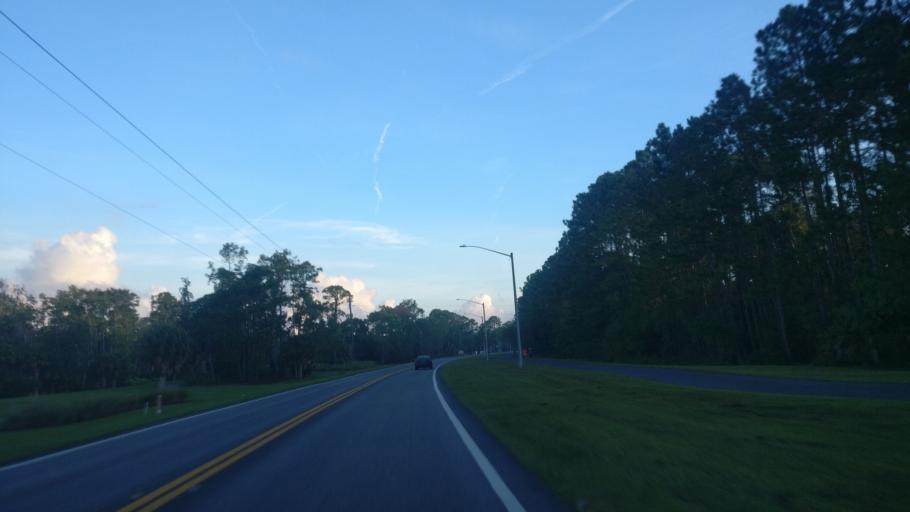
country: US
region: Florida
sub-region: Flagler County
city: Palm Coast
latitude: 29.5345
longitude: -81.2388
